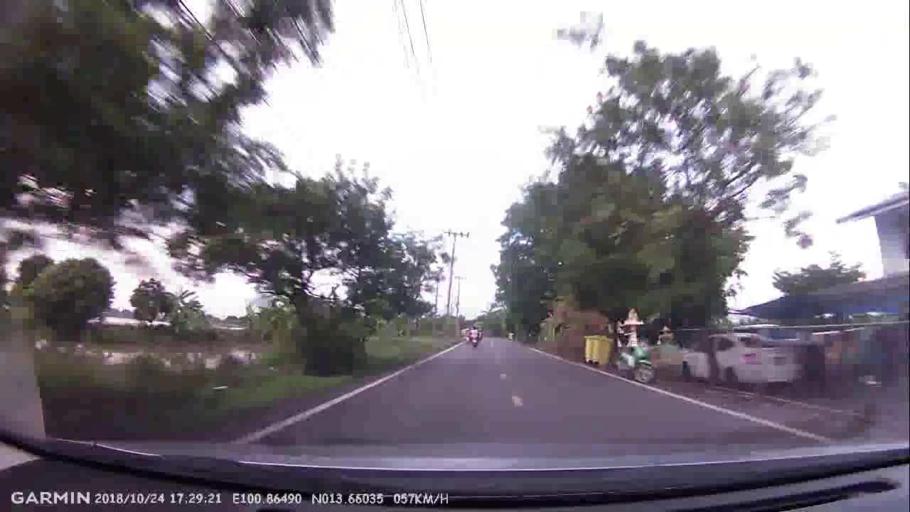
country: TH
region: Samut Prakan
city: Ban Khlong Bang Sao Thong
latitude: 13.6605
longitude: 100.8649
